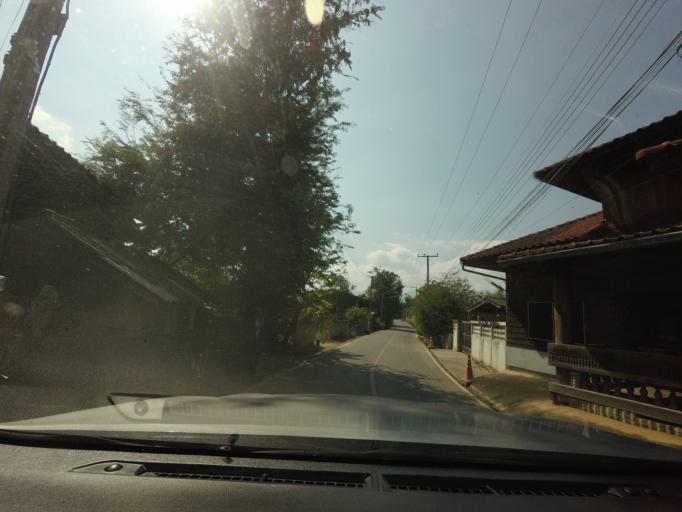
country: TH
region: Mae Hong Son
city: Wiang Nuea
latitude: 19.3934
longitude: 98.4436
